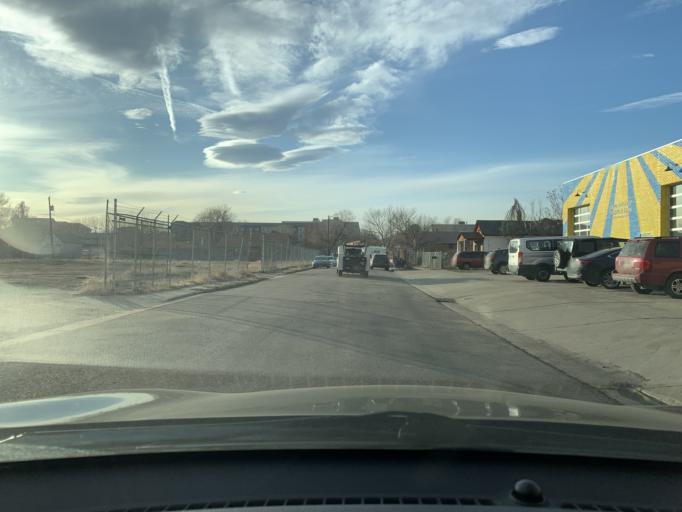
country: US
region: Colorado
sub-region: Denver County
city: Denver
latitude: 39.7356
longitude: -105.0196
